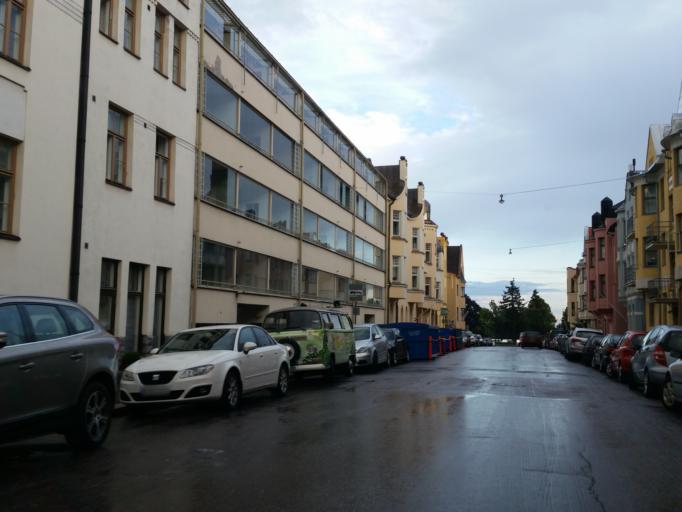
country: FI
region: Uusimaa
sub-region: Helsinki
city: Helsinki
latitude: 60.1566
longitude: 24.9434
